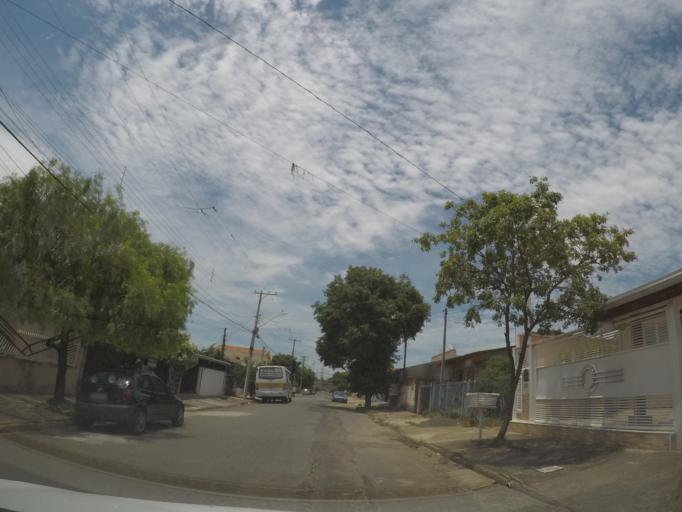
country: BR
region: Sao Paulo
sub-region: Hortolandia
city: Hortolandia
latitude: -22.8412
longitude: -47.1914
